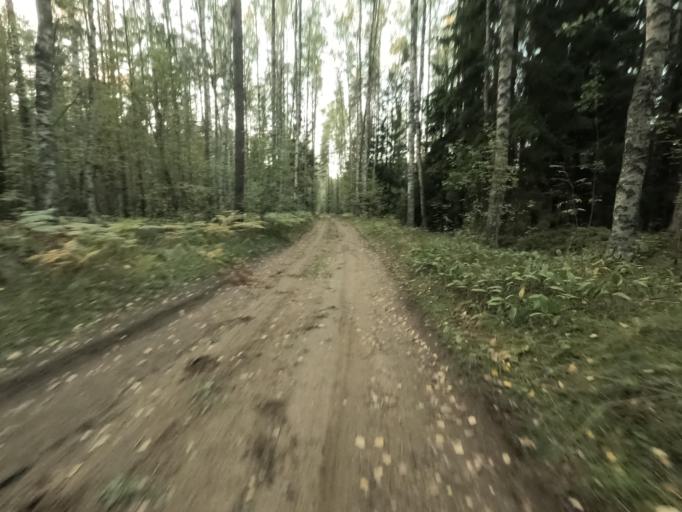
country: RU
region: Leningrad
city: Otradnoye
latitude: 59.8346
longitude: 30.8085
